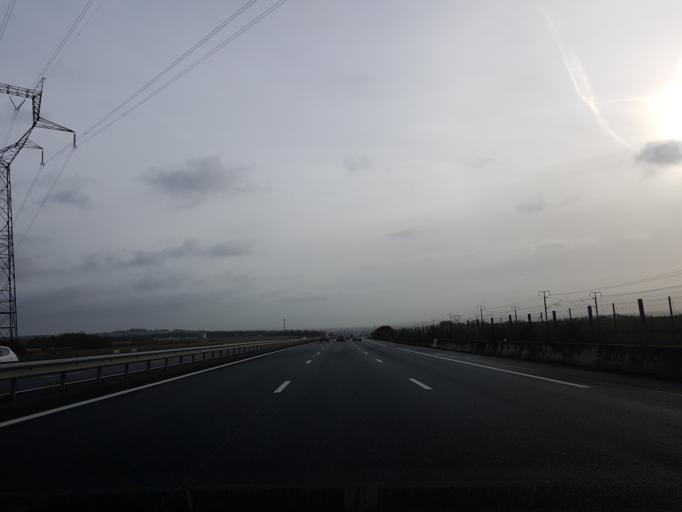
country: FR
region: Ile-de-France
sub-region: Departement de Seine-et-Marne
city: Montereau-Fault-Yonne
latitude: 48.4111
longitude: 2.9571
